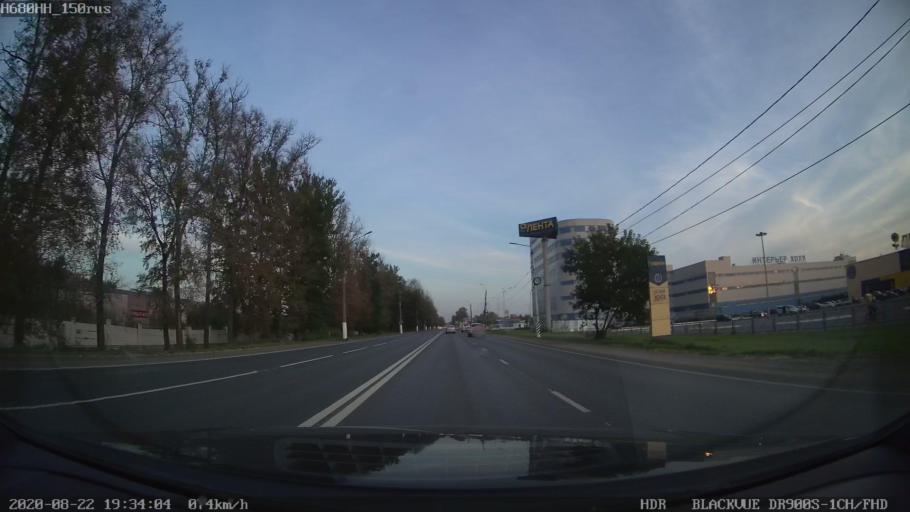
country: RU
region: Tverskaya
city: Tver
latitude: 56.8444
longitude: 35.9499
